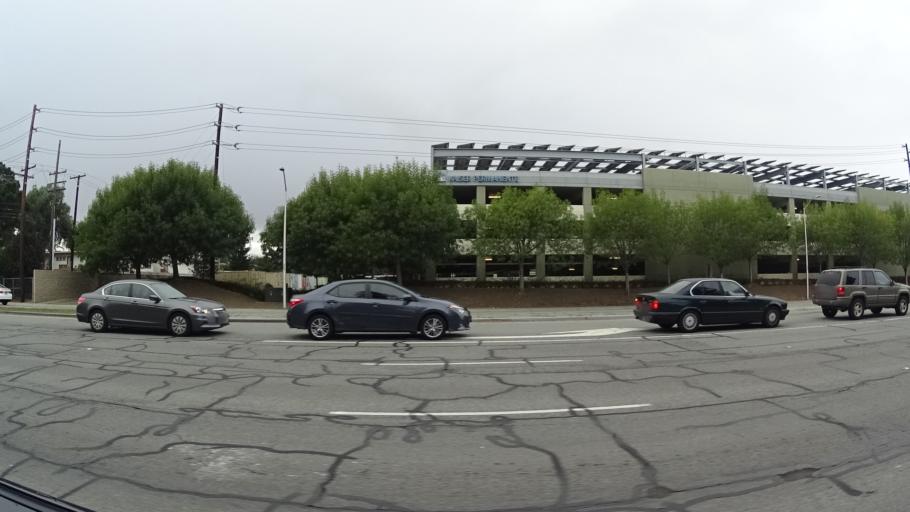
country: US
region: California
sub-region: Santa Clara County
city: Cupertino
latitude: 37.3343
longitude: -121.9955
